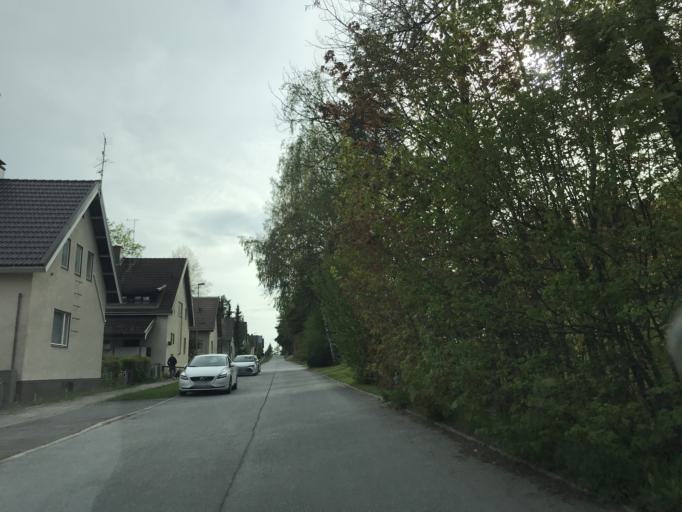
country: FI
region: Varsinais-Suomi
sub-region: Turku
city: Turku
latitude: 60.4591
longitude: 22.3191
